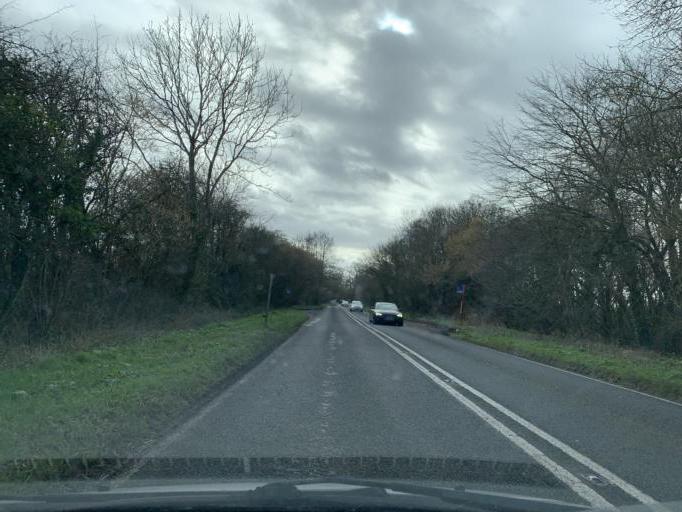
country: GB
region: England
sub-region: Wiltshire
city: Downton
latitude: 50.9776
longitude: -1.7642
